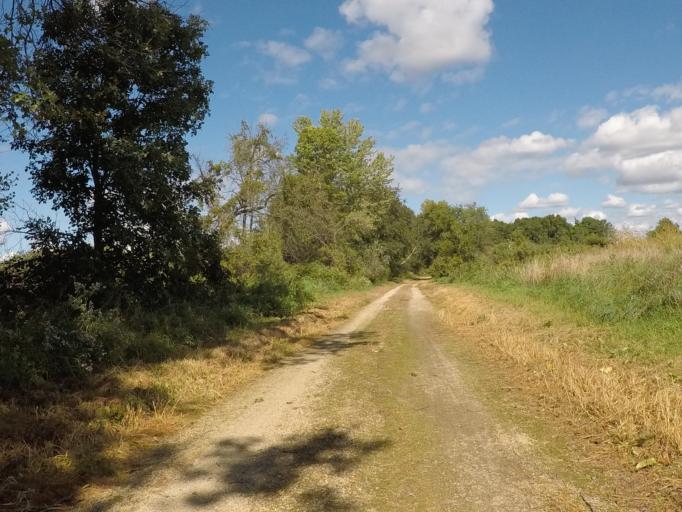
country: US
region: Wisconsin
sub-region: Richland County
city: Richland Center
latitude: 43.2442
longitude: -90.3049
